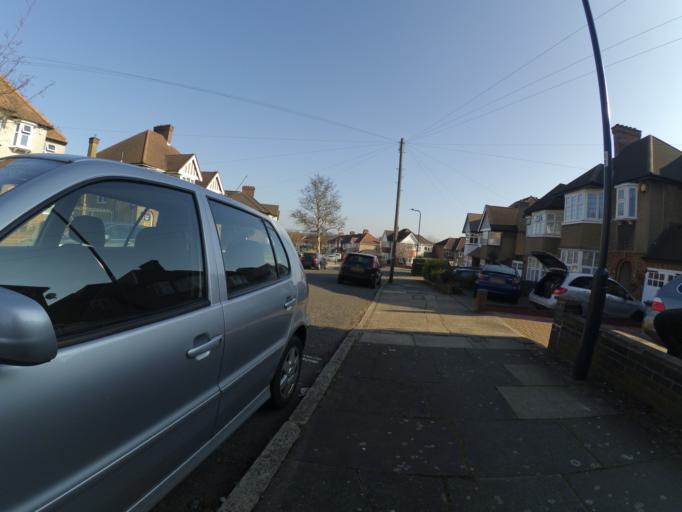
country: GB
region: England
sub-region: Greater London
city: Wembley
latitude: 51.5726
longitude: -0.2667
